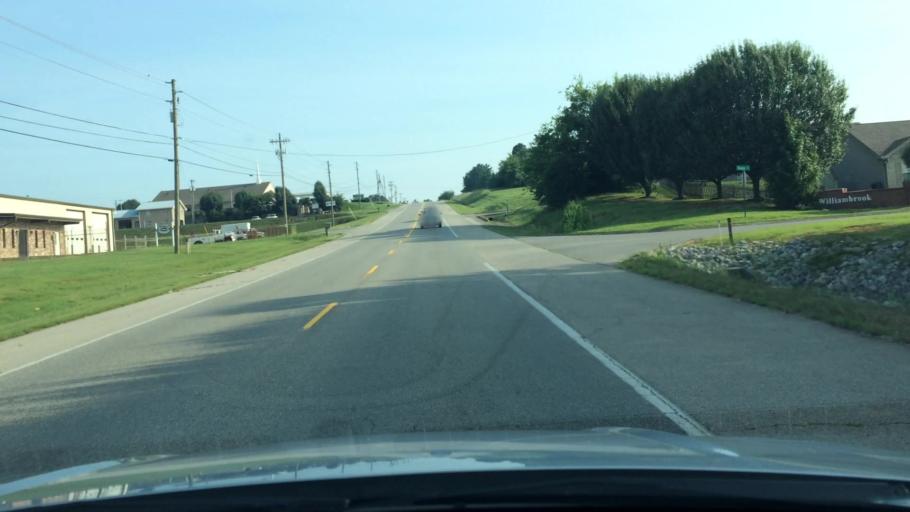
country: US
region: Tennessee
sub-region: Blount County
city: Louisville
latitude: 35.7496
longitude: -84.0443
